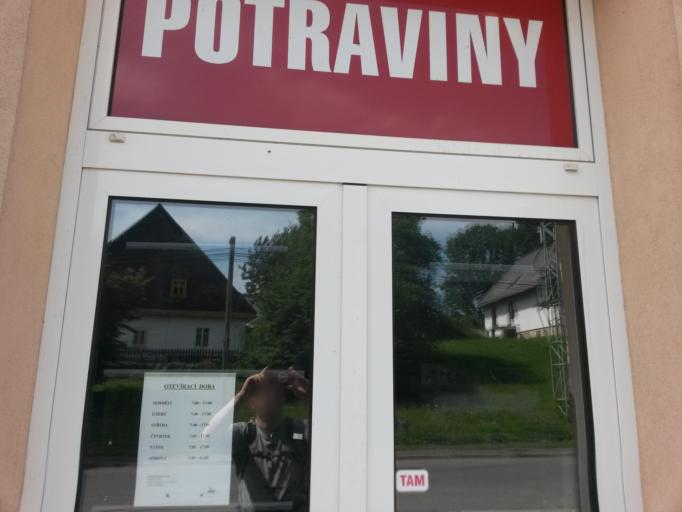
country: CZ
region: Kralovehradecky
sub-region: Okres Nachod
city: Police nad Metuji
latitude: 50.5405
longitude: 16.2658
